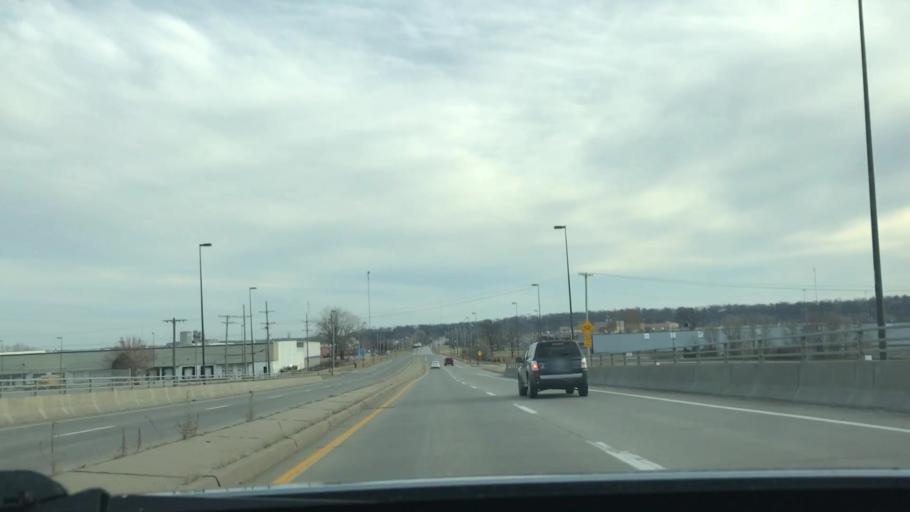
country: US
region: Missouri
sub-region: Clay County
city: North Kansas City
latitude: 39.1402
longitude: -94.5304
